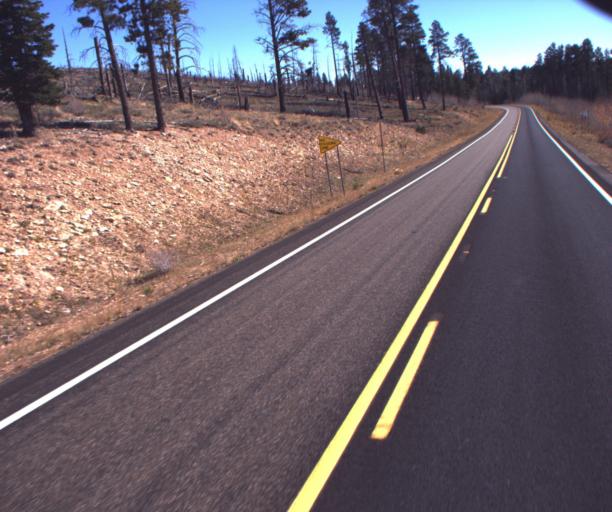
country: US
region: Arizona
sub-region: Coconino County
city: Grand Canyon
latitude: 36.5452
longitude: -112.1785
